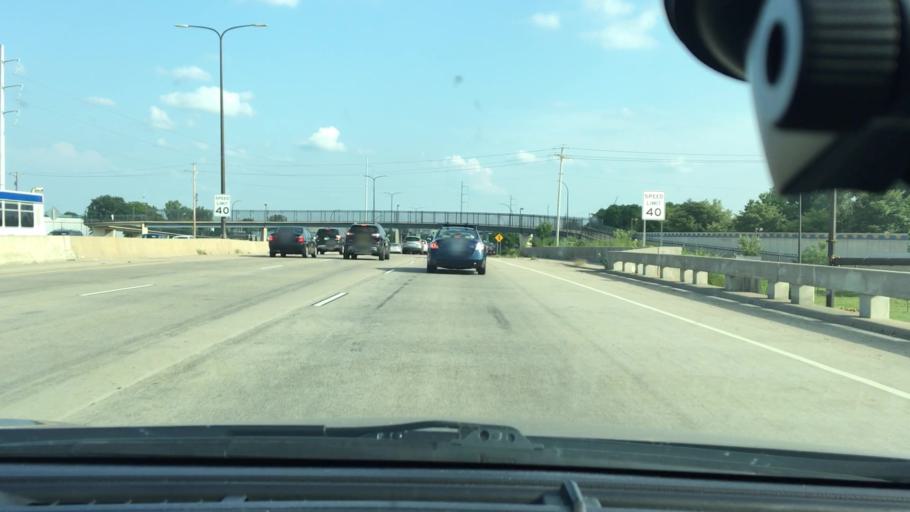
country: US
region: Minnesota
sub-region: Hennepin County
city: Minneapolis
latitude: 44.9599
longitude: -93.2469
